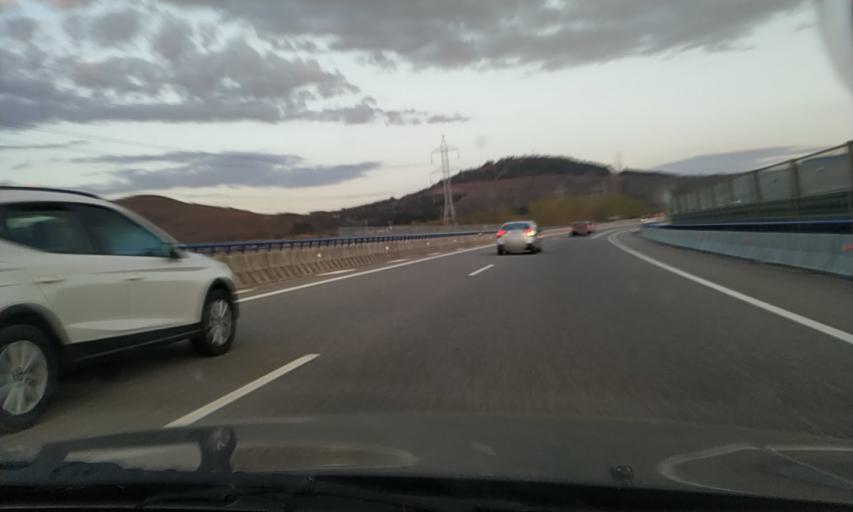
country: ES
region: Castille and Leon
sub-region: Provincia de Leon
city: Ponferrada
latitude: 42.5822
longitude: -6.6097
